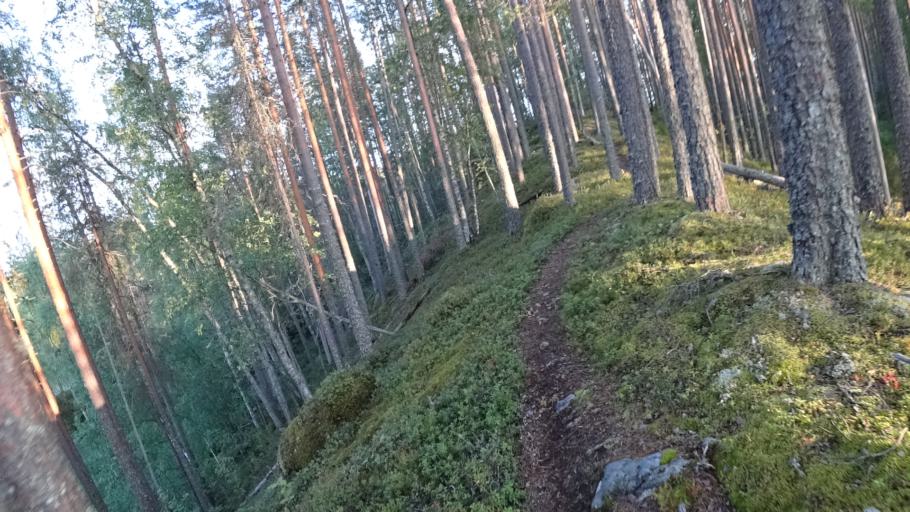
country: FI
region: North Karelia
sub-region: Joensuu
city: Ilomantsi
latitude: 62.5854
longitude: 31.1880
